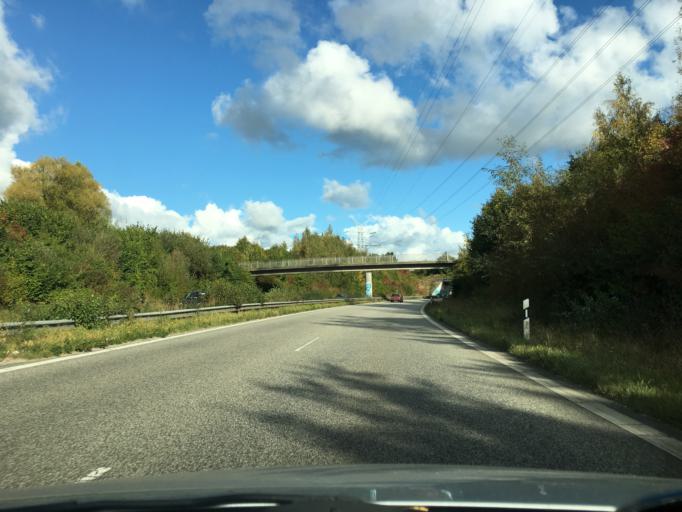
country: DE
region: Schleswig-Holstein
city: Monkeberg
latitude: 54.3360
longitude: 10.2052
